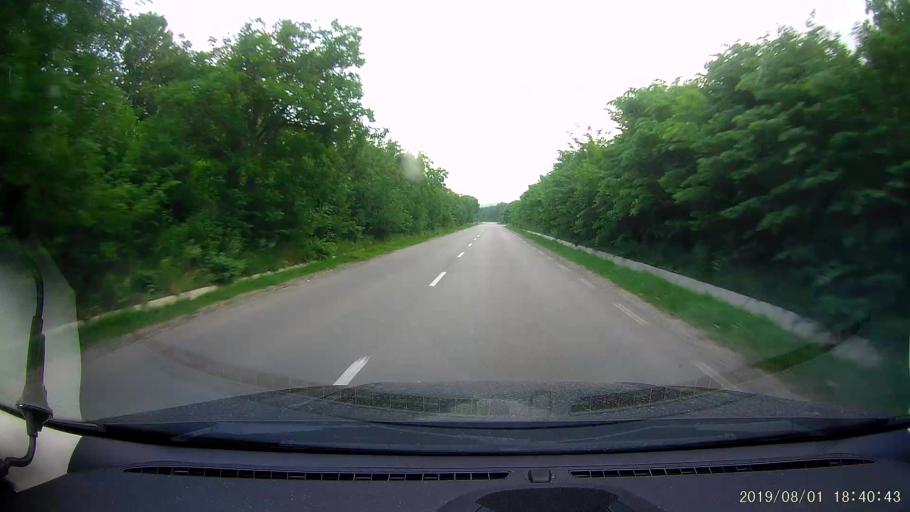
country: BG
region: Shumen
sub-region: Obshtina Khitrino
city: Gara Khitrino
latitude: 43.3606
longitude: 26.9205
